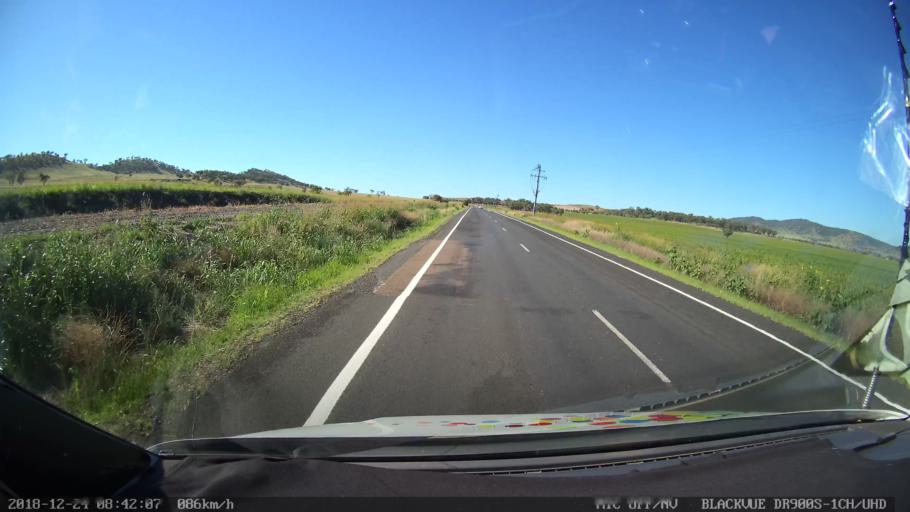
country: AU
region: New South Wales
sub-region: Liverpool Plains
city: Quirindi
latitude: -31.3702
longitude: 150.6435
